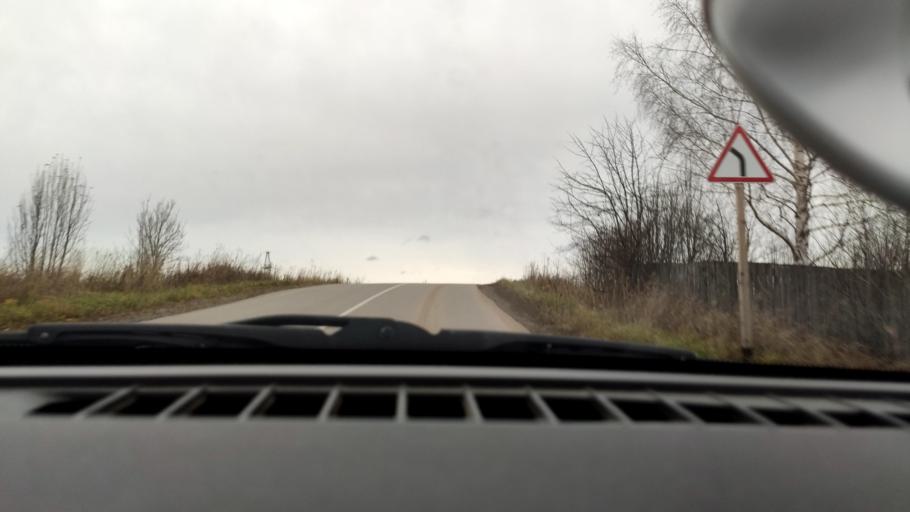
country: RU
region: Perm
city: Ferma
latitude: 57.9258
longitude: 56.3319
